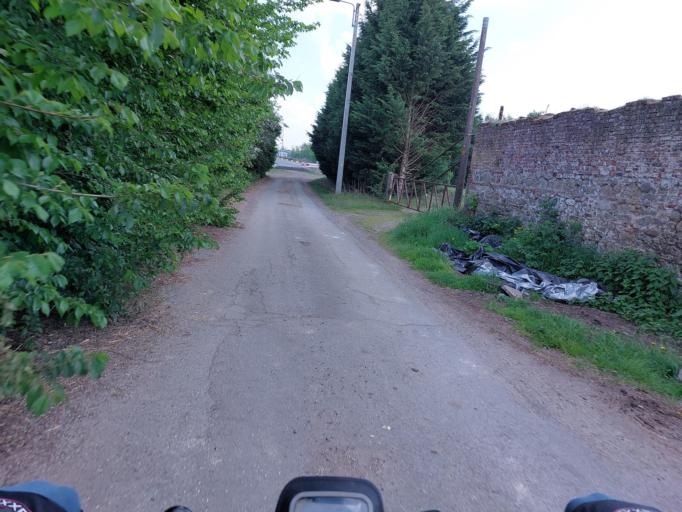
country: BE
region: Wallonia
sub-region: Province du Hainaut
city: Quaregnon
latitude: 50.4722
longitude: 3.8553
